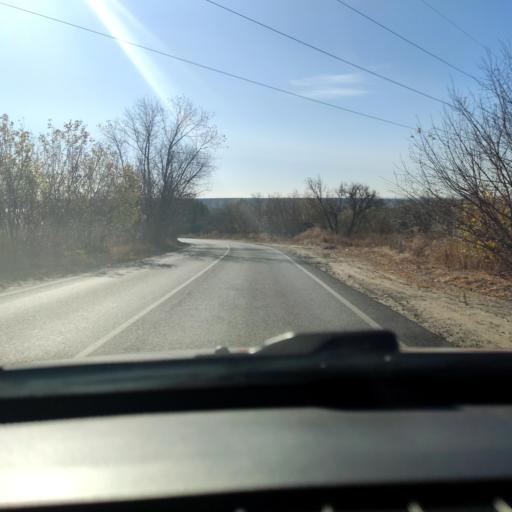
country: RU
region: Voronezj
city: Shilovo
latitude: 51.5537
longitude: 39.1324
